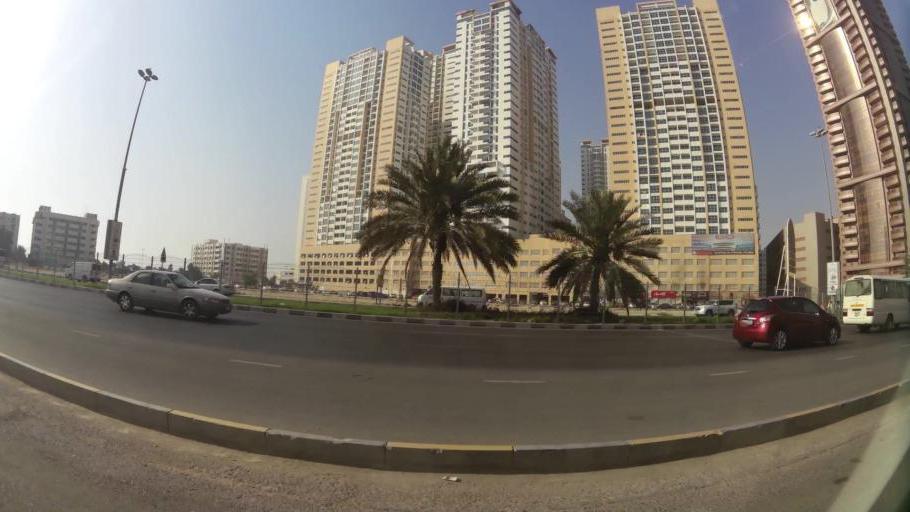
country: AE
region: Ajman
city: Ajman
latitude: 25.3930
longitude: 55.4296
